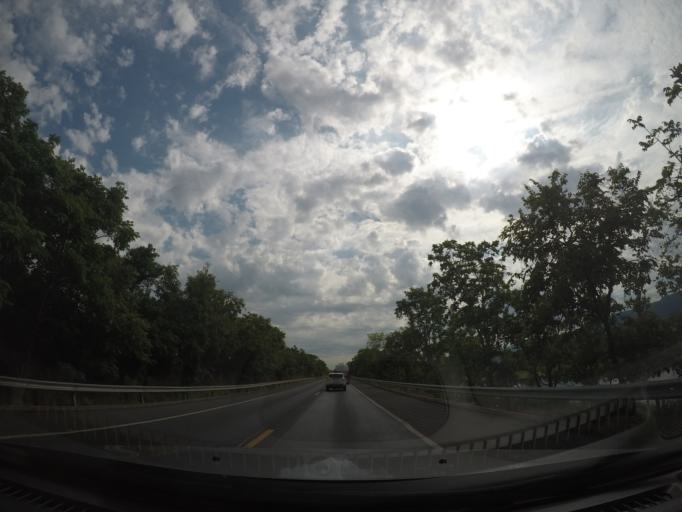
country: BR
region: Goias
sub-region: Formosa
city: Formosa
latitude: -14.9167
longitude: -46.9536
